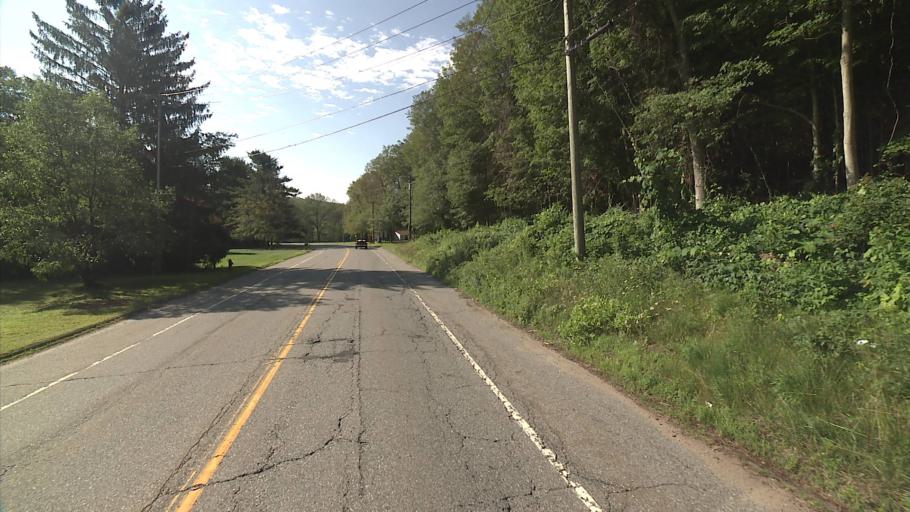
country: US
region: Connecticut
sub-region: New London County
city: Montville Center
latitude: 41.5603
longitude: -72.1645
